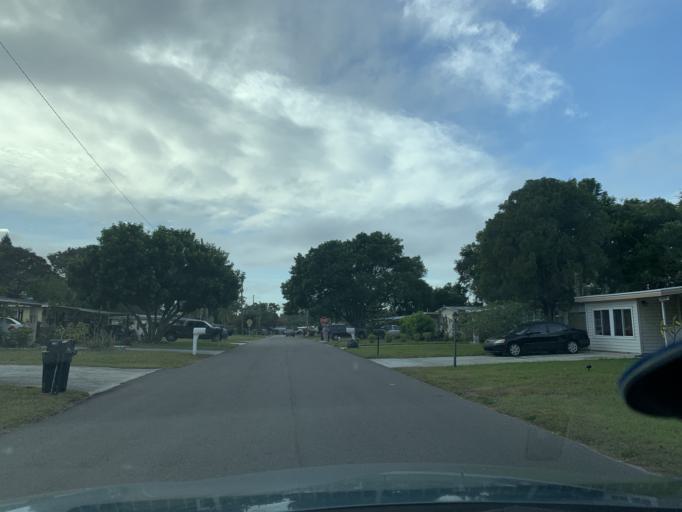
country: US
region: Florida
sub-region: Pinellas County
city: Ridgecrest
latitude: 27.8785
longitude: -82.7863
